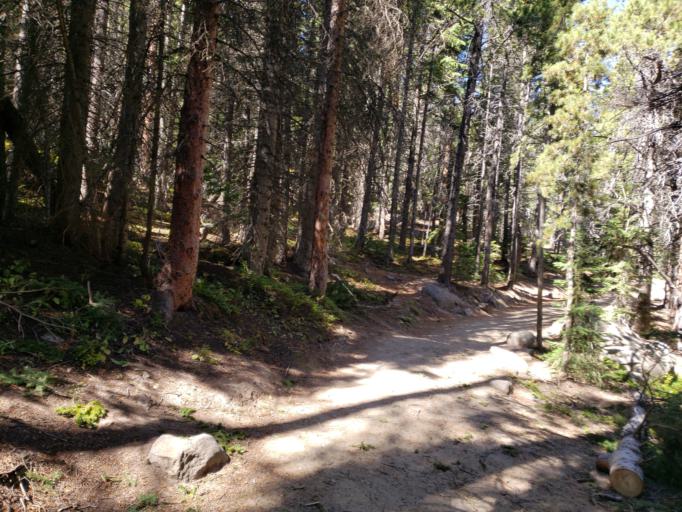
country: US
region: Colorado
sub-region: Larimer County
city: Estes Park
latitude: 40.3108
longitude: -105.6459
